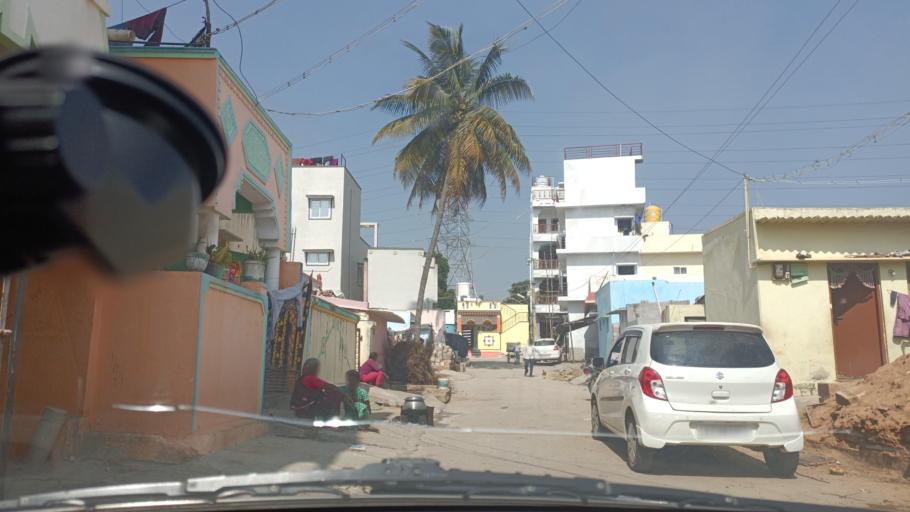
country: IN
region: Karnataka
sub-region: Bangalore Rural
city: Devanhalli
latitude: 13.1833
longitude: 77.6429
